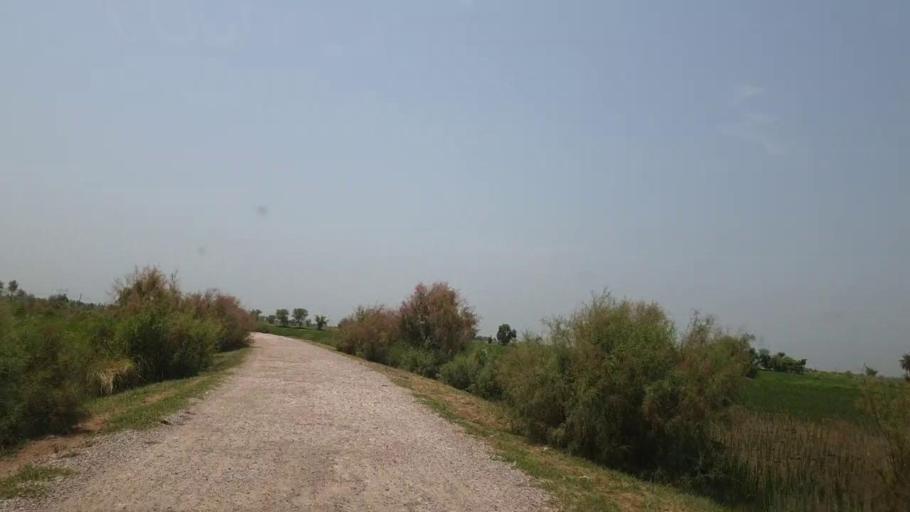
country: PK
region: Sindh
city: Shikarpur
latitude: 27.9005
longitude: 68.6322
